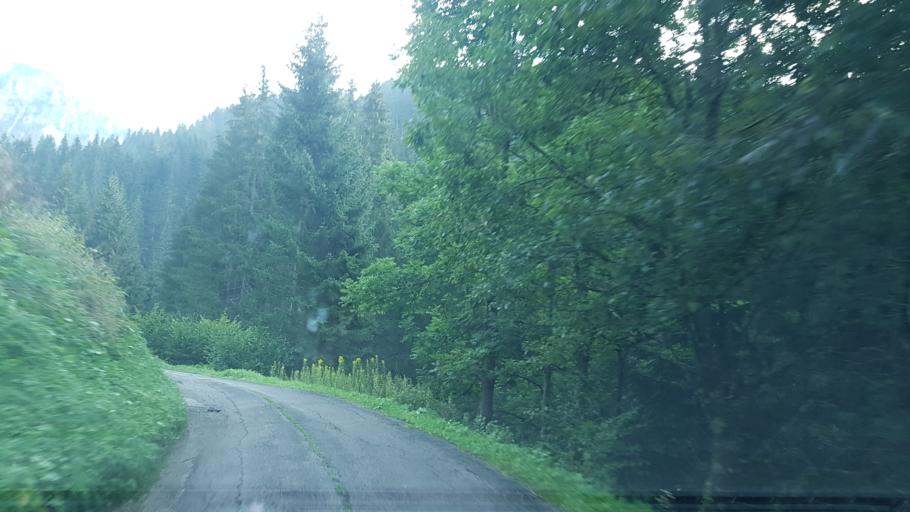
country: IT
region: Veneto
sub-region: Provincia di Belluno
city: San Pietro di Cadore
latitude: 46.5905
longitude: 12.5807
